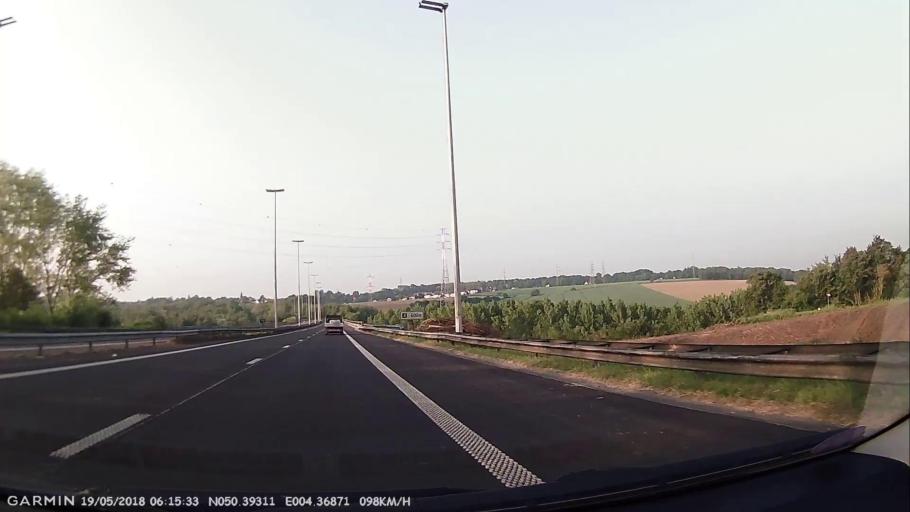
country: BE
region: Wallonia
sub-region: Province du Hainaut
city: Courcelles
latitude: 50.3928
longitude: 4.3688
